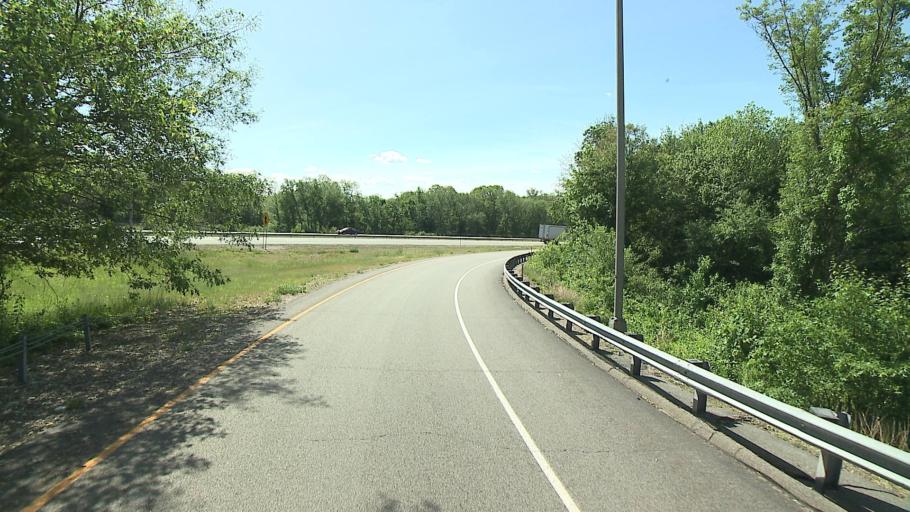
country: US
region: Connecticut
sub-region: New London County
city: Montville Center
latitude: 41.4899
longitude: -72.1151
